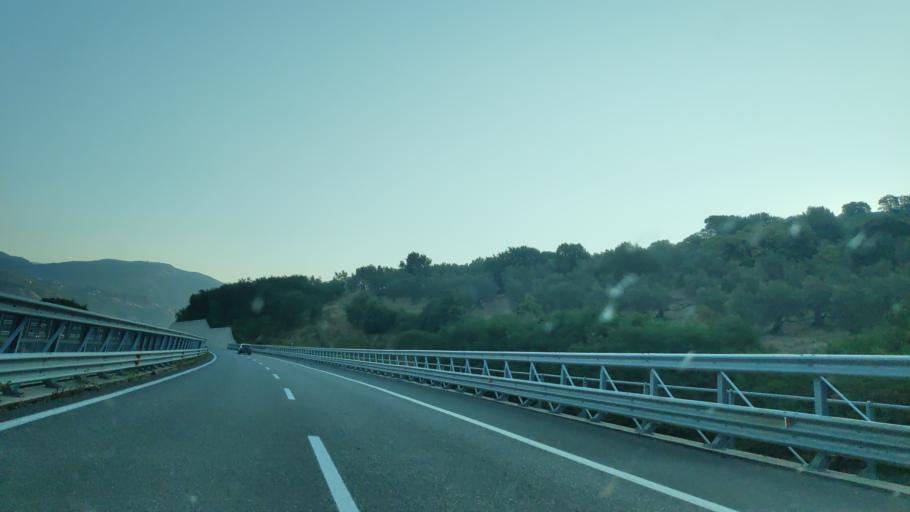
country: IT
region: Calabria
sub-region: Provincia di Catanzaro
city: Nocera Terinese
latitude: 39.0433
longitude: 16.1454
